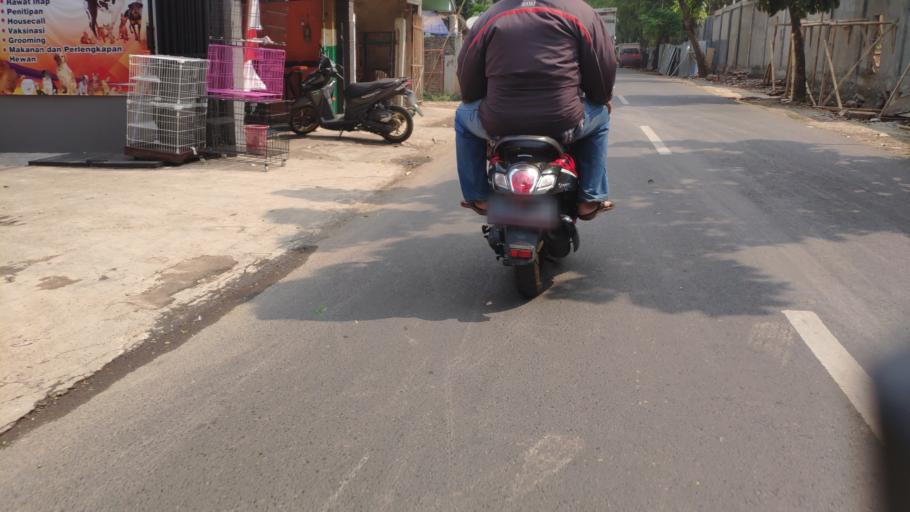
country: ID
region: West Java
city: Depok
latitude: -6.3146
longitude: 106.8254
